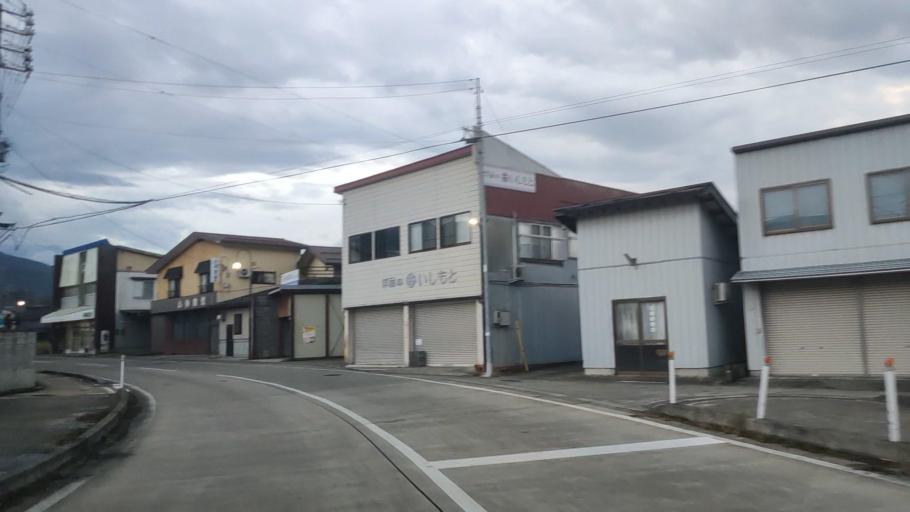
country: JP
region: Nagano
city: Iiyama
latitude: 36.8612
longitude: 138.4051
